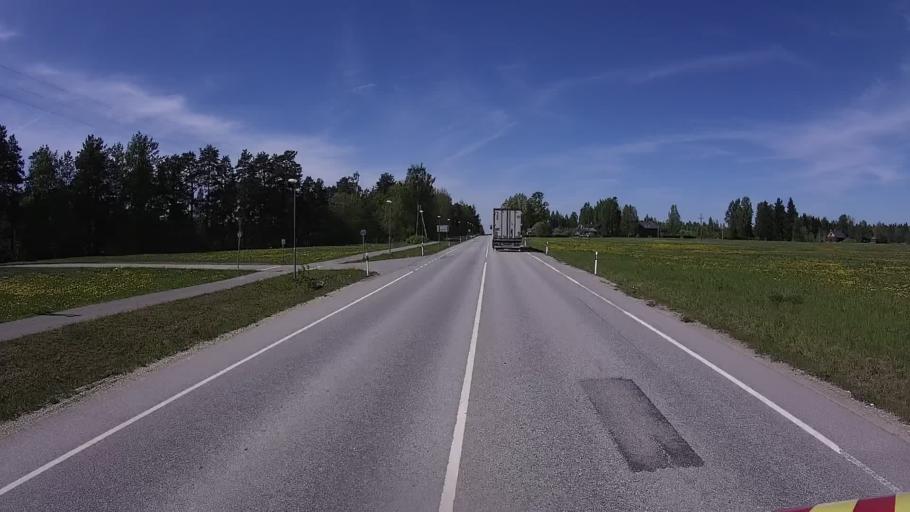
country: EE
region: Vorumaa
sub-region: Voru linn
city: Voru
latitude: 57.8112
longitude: 27.0569
